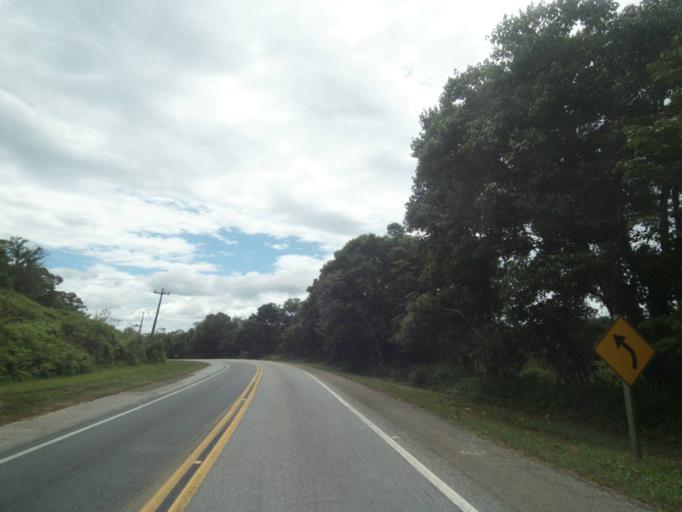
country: BR
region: Parana
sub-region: Antonina
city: Antonina
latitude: -25.4485
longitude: -48.7733
